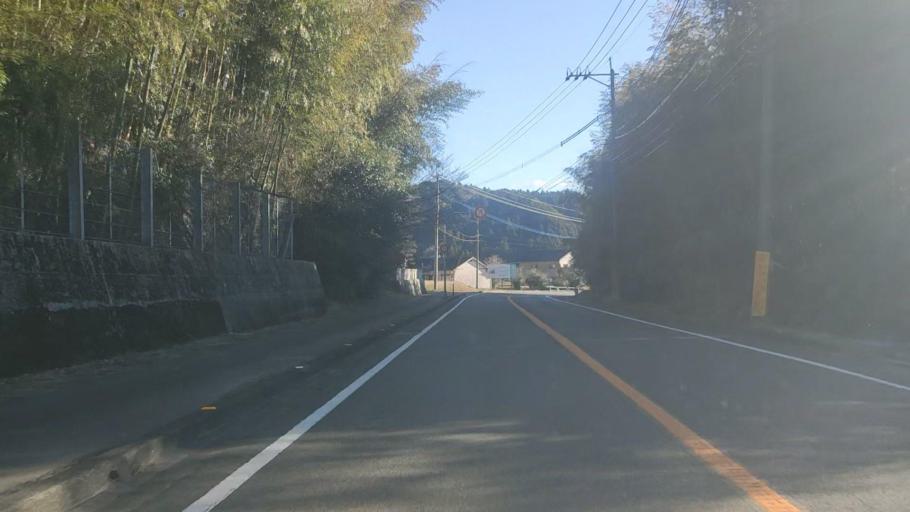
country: JP
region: Fukuoka
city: Maebaru-chuo
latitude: 33.4545
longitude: 130.2758
